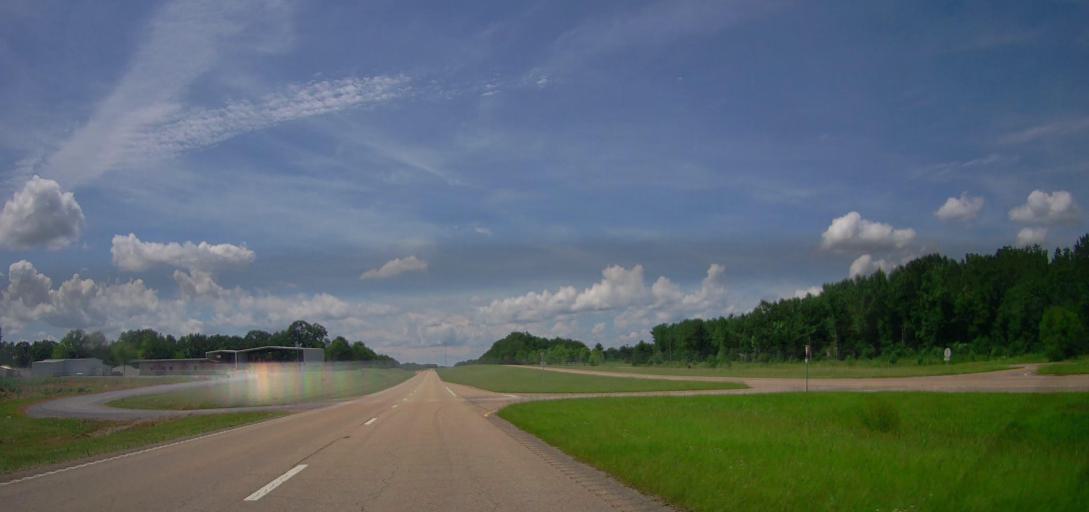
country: US
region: Mississippi
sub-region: Lee County
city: Nettleton
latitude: 33.9886
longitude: -88.6219
